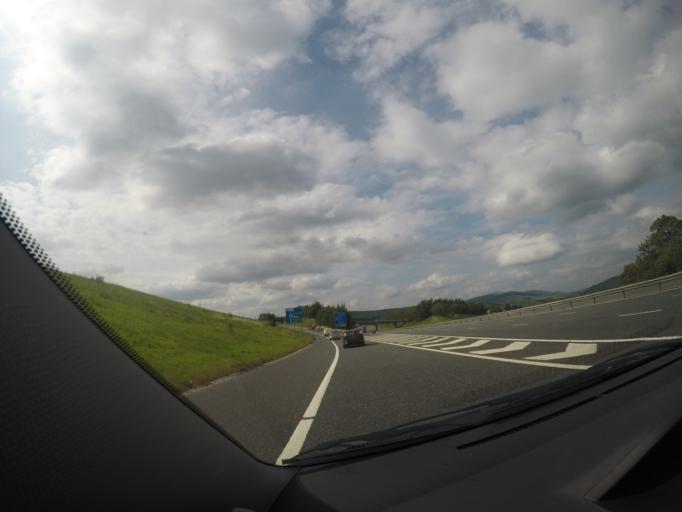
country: GB
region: Scotland
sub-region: South Lanarkshire
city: Douglas
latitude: 55.5011
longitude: -3.6949
